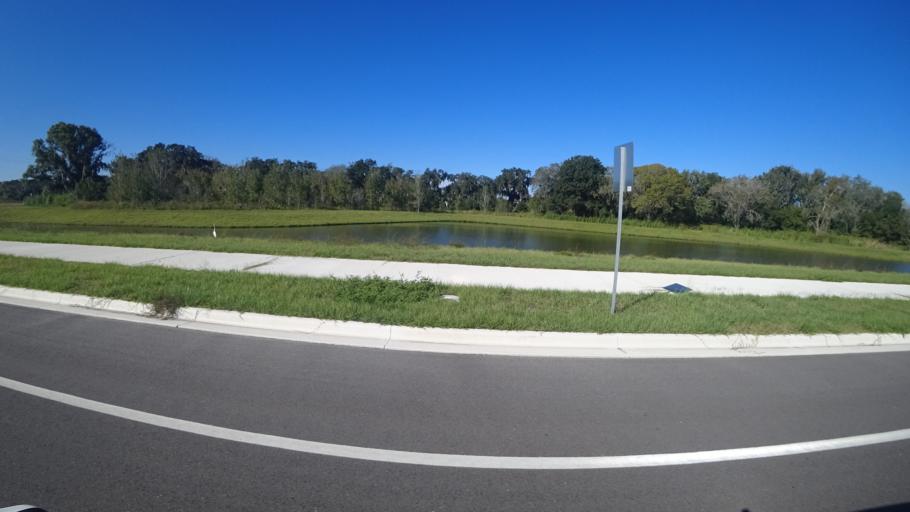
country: US
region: Florida
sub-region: Manatee County
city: Ellenton
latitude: 27.5807
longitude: -82.4356
